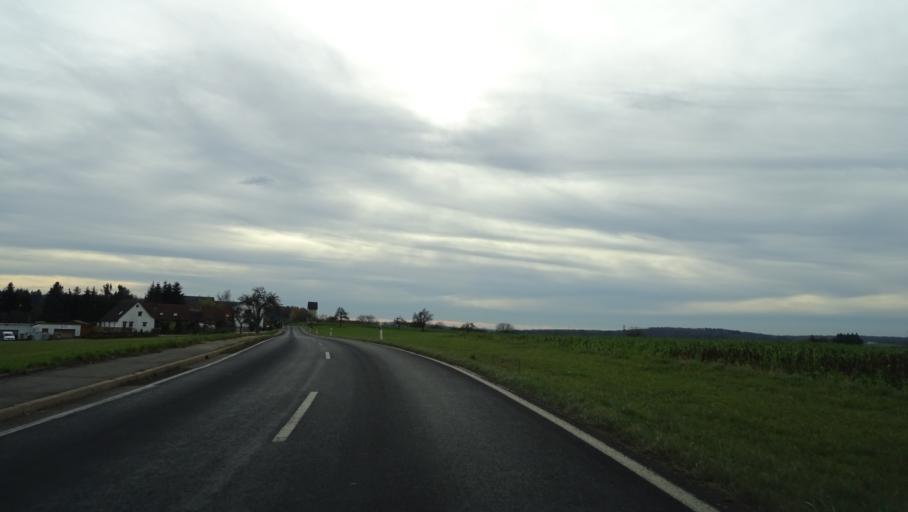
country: DE
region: Baden-Wuerttemberg
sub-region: Karlsruhe Region
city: Fahrenbach
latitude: 49.4130
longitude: 9.1572
